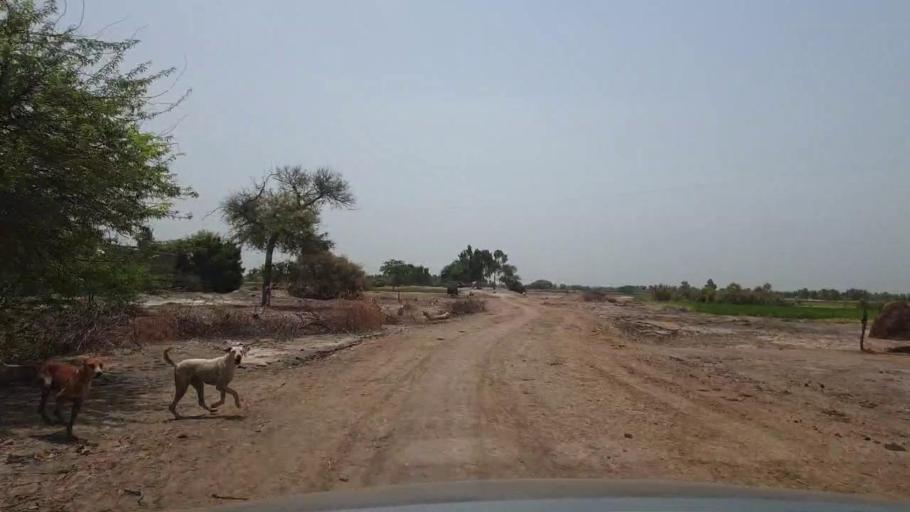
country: PK
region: Sindh
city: Madeji
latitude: 27.7735
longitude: 68.4057
